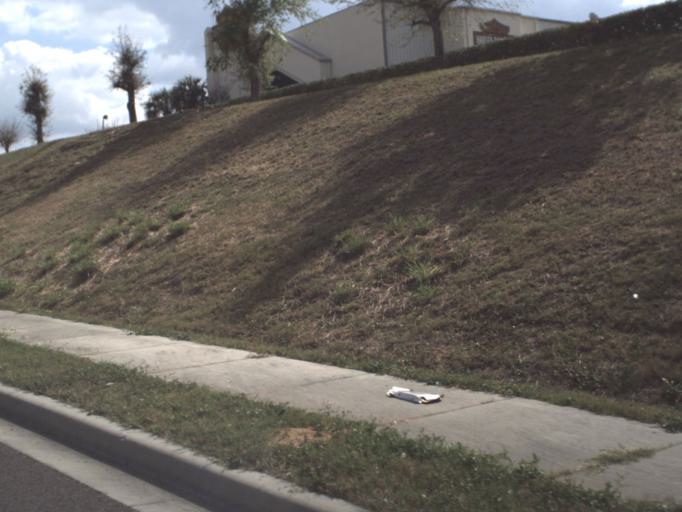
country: US
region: Florida
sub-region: Lake County
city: Clermont
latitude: 28.5372
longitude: -81.7379
